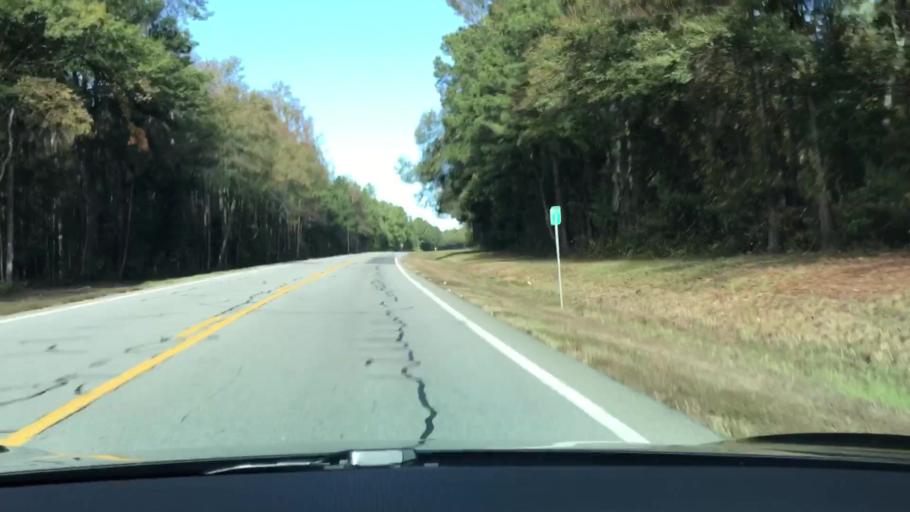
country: US
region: Georgia
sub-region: Warren County
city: Warrenton
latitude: 33.3478
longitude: -82.5830
